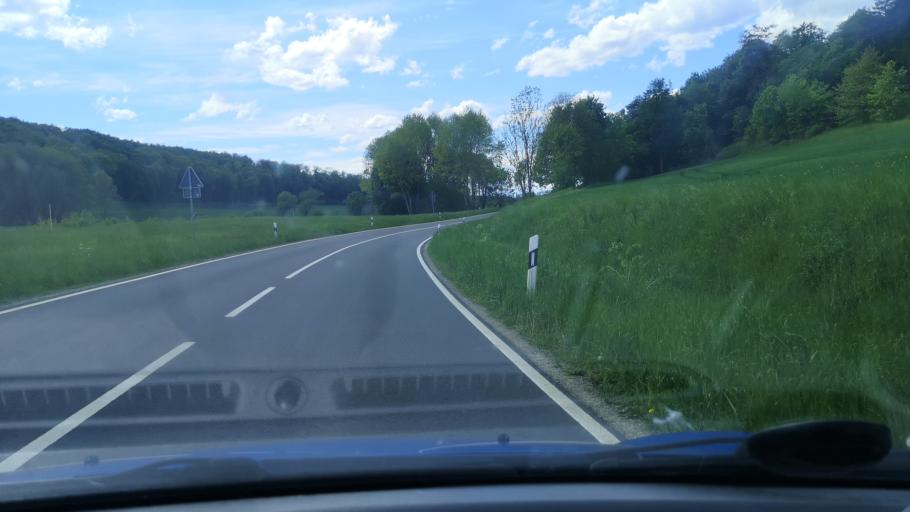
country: DE
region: Lower Saxony
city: Hardegsen
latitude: 51.5853
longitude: 9.8267
